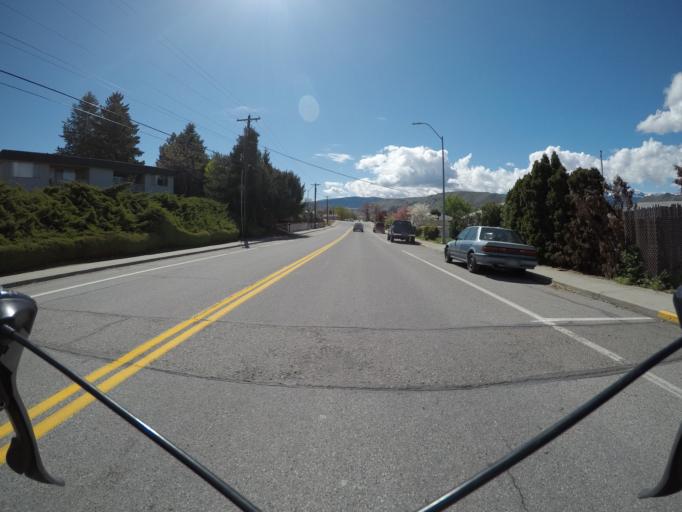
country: US
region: Washington
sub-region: Douglas County
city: East Wenatchee
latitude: 47.4177
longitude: -120.2917
